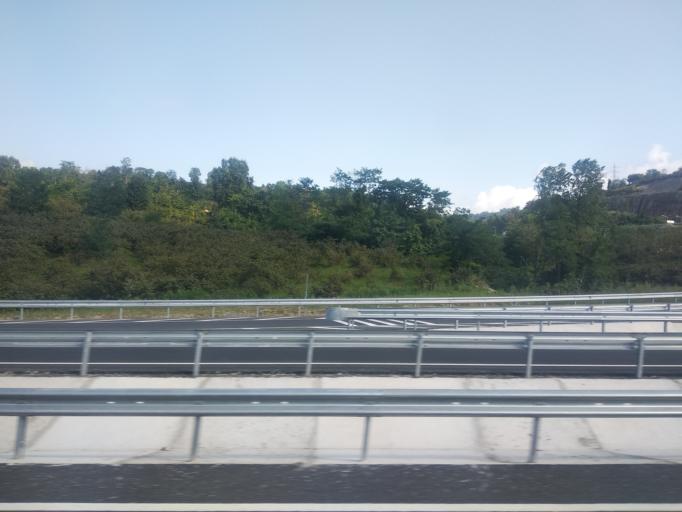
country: TR
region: Ordu
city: Ordu
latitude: 40.9907
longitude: 37.8139
